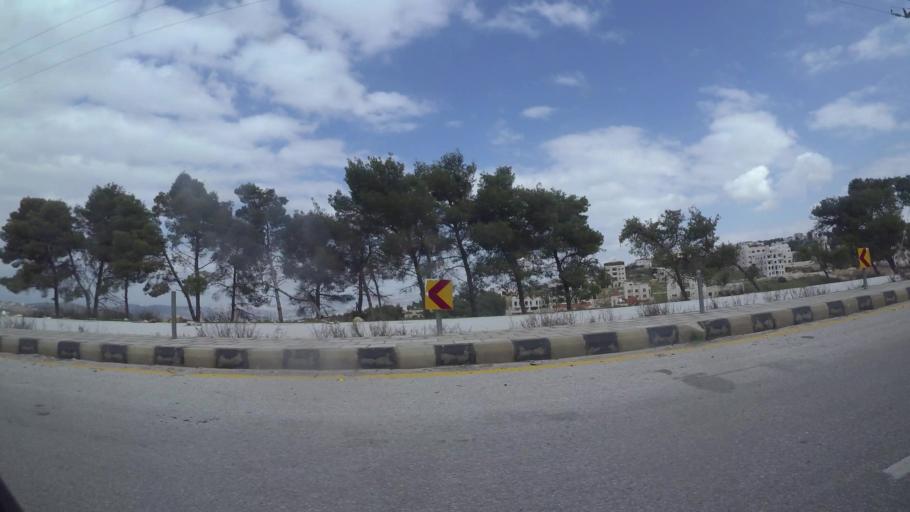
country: JO
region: Amman
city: Al Jubayhah
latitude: 32.0304
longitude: 35.7961
